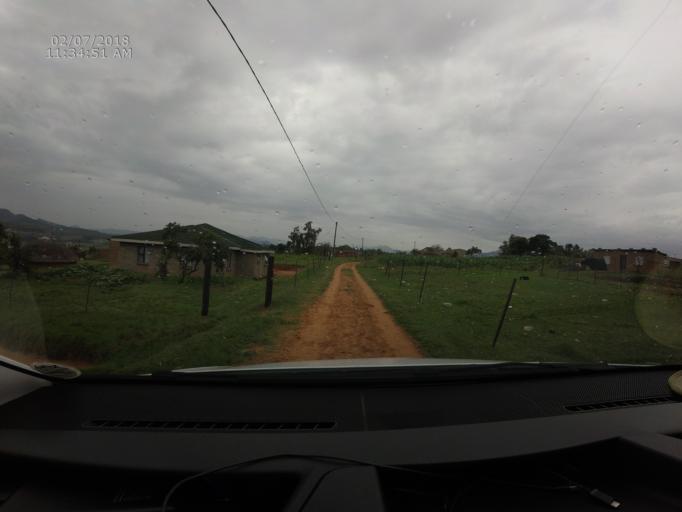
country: LS
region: Berea
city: Teyateyaneng
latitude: -29.1059
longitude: 27.9644
